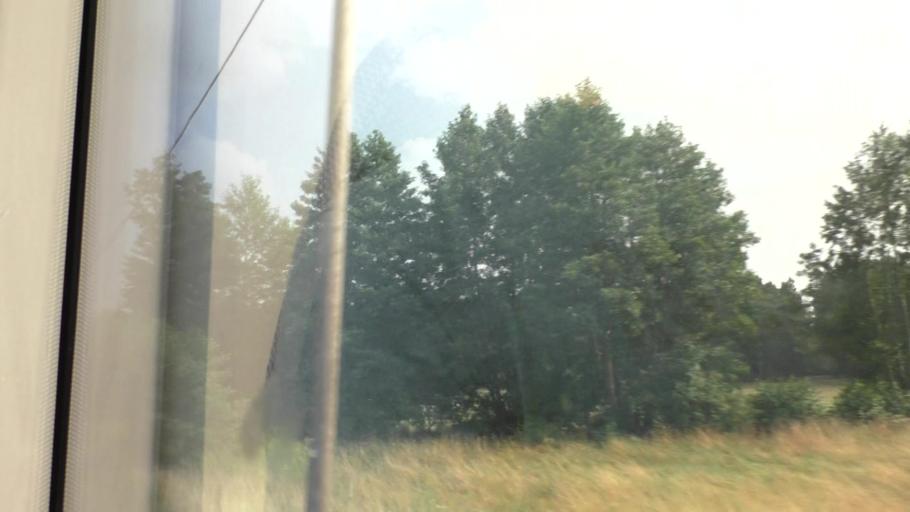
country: DE
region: Brandenburg
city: Spreenhagen
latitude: 52.2836
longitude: 13.8294
